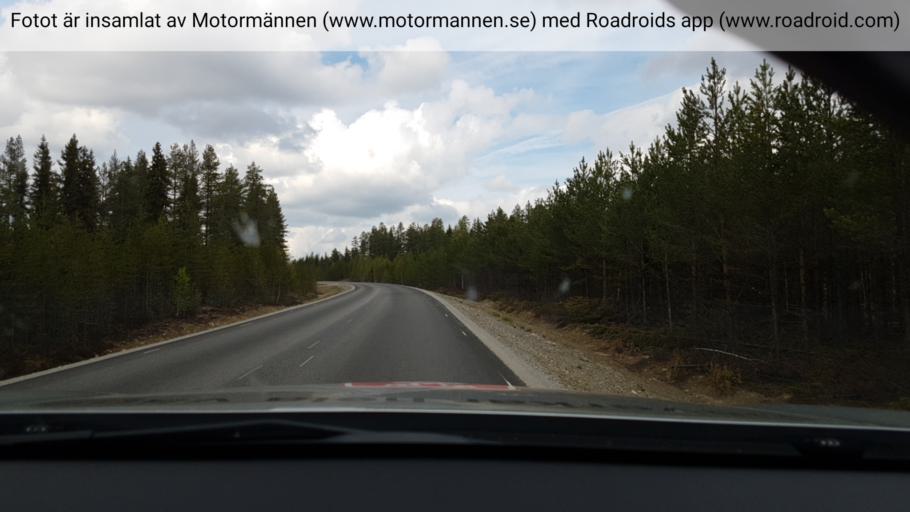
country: SE
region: Vaesterbotten
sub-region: Lycksele Kommun
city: Lycksele
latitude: 64.0216
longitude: 18.4504
